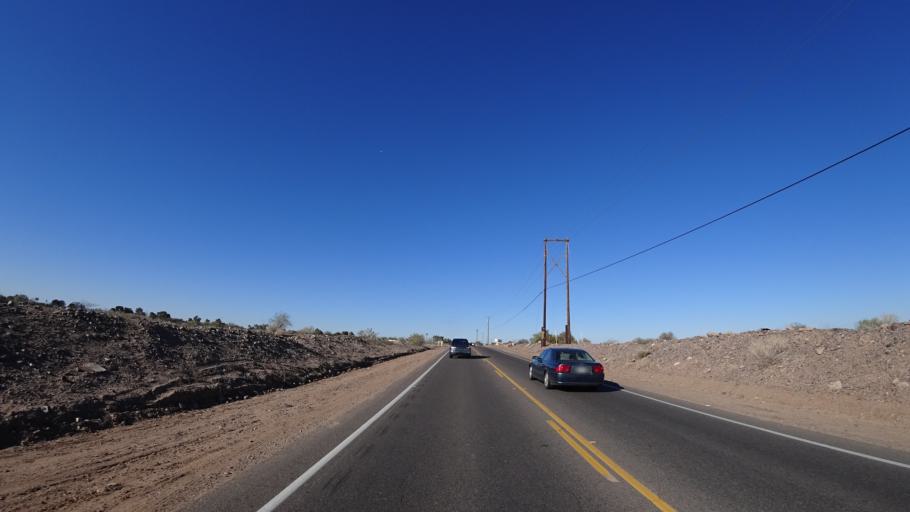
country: US
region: Arizona
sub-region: Maricopa County
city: Laveen
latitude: 33.3987
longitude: -112.2038
